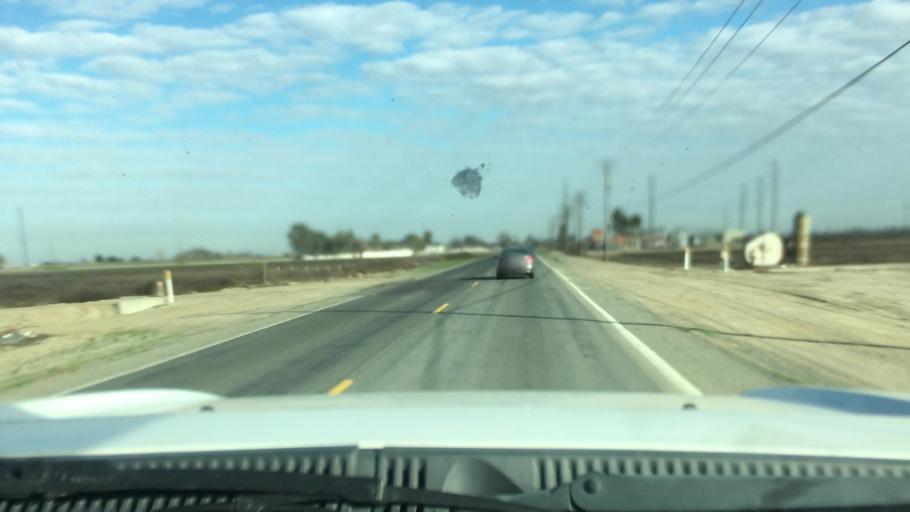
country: US
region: California
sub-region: Kings County
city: Stratford
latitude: 36.2205
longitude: -119.7803
